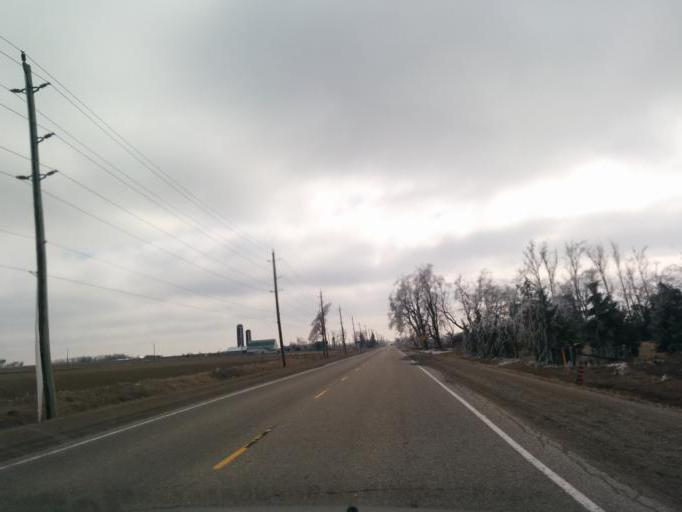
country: CA
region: Ontario
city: Waterloo
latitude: 43.6269
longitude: -80.5512
